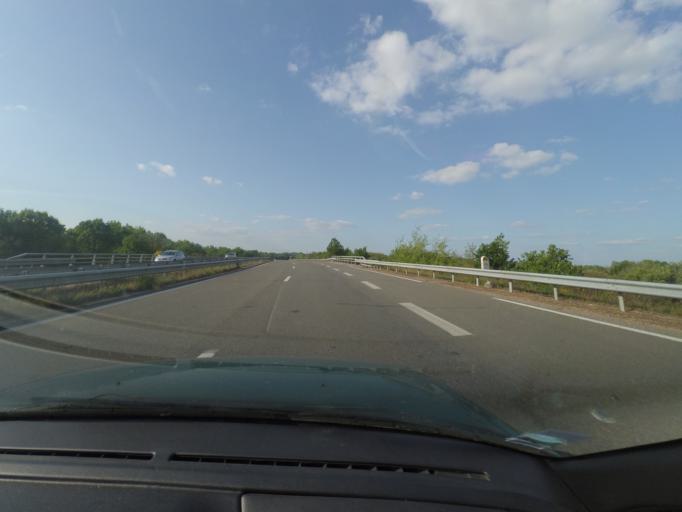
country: FR
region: Pays de la Loire
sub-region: Departement de la Vendee
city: Saligny
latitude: 46.8359
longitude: -1.4200
